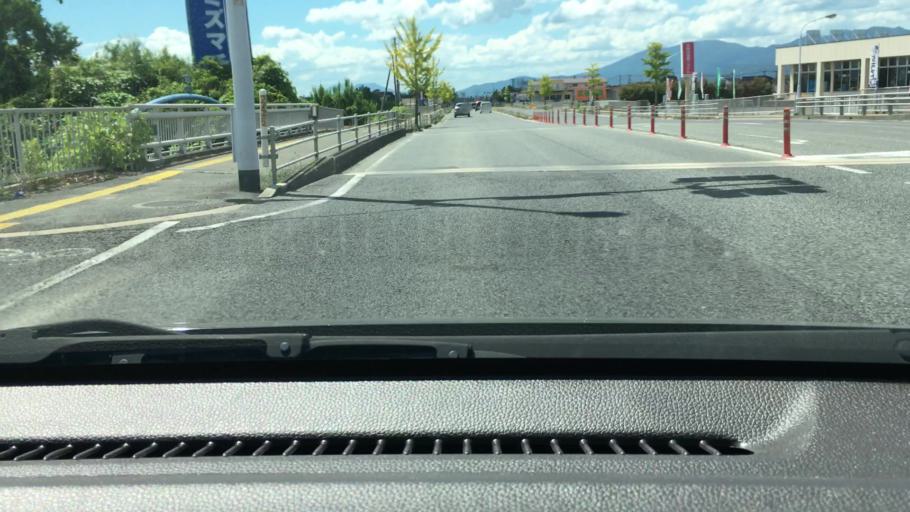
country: JP
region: Saga Prefecture
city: Saga-shi
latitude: 33.2743
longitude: 130.3297
